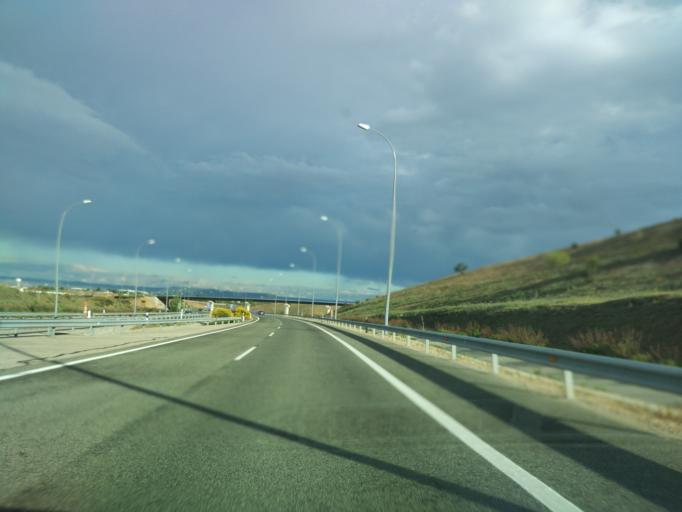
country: ES
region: Madrid
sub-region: Provincia de Madrid
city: Ajalvir
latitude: 40.5118
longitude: -3.4978
